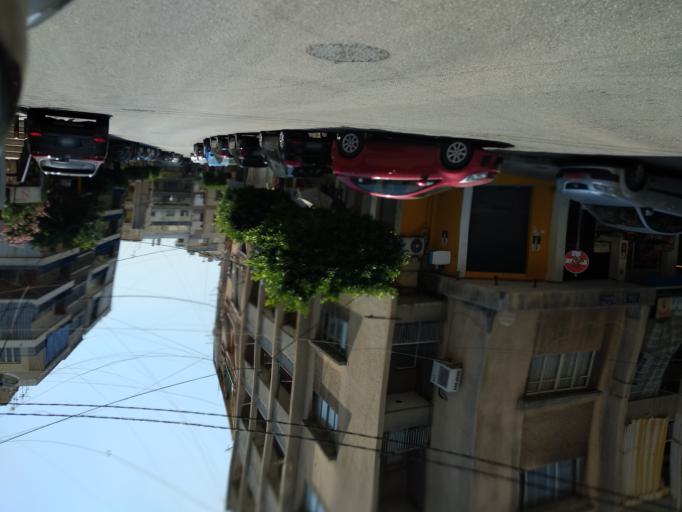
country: LB
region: Beyrouth
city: Beirut
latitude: 33.8921
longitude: 35.5301
